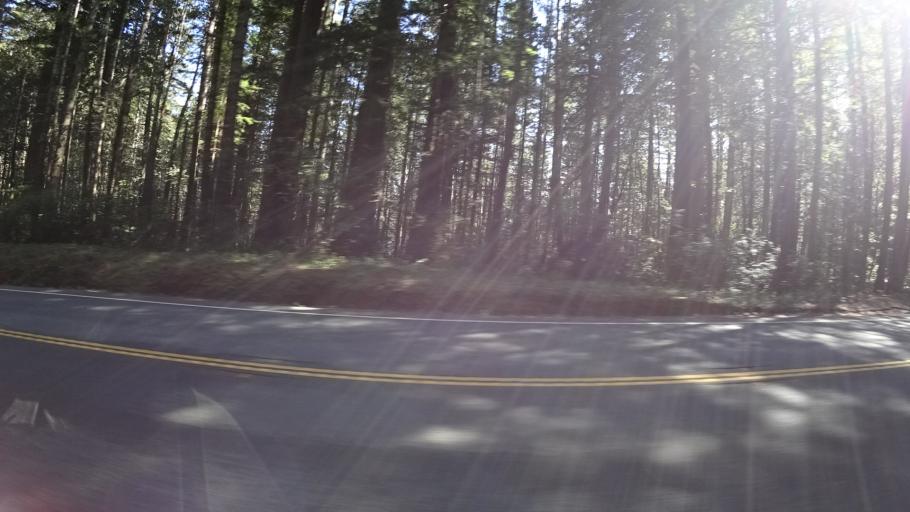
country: US
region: California
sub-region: Del Norte County
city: Bertsch-Oceanview
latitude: 41.6917
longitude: -124.1077
